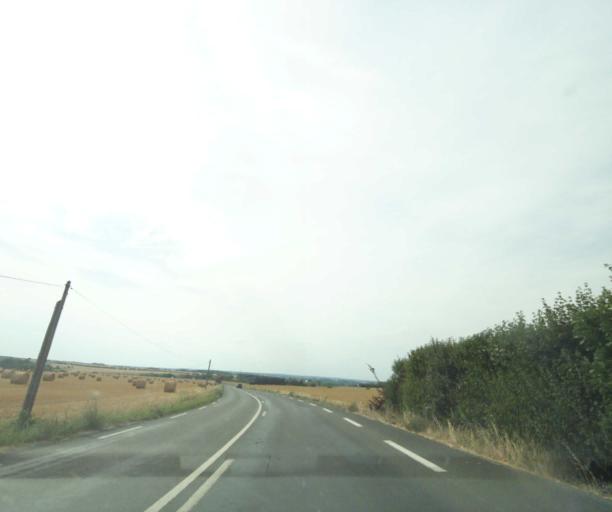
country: FR
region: Centre
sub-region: Departement d'Indre-et-Loire
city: Saint-Christophe-sur-le-Nais
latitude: 47.6541
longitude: 0.4895
